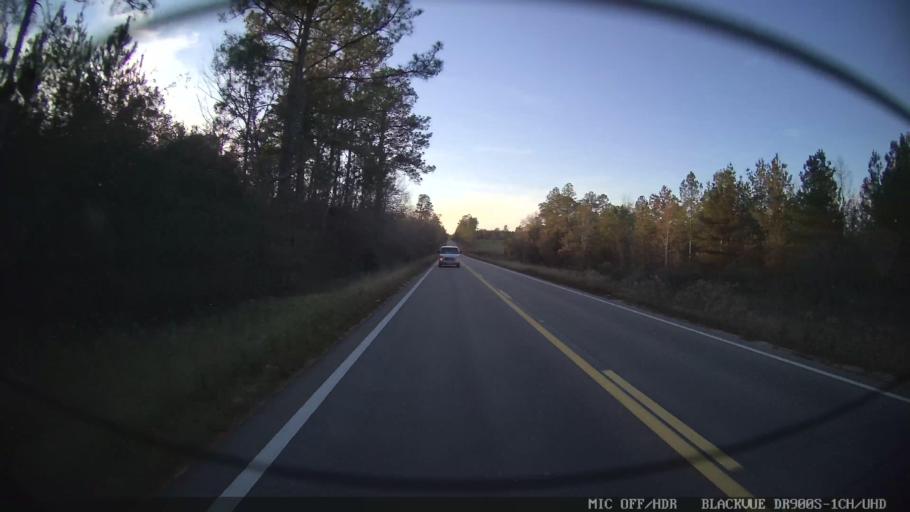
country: US
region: Mississippi
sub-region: Lamar County
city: Lumberton
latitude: 30.9974
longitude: -89.2973
